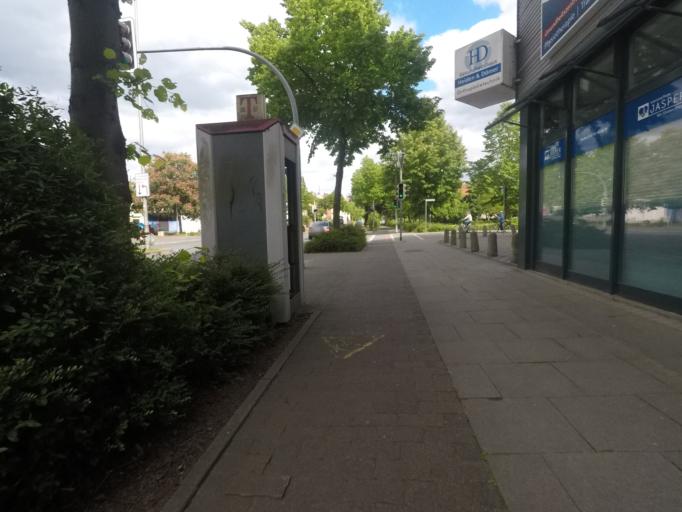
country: DE
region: North Rhine-Westphalia
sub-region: Regierungsbezirk Detmold
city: Herford
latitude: 52.1217
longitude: 8.6757
